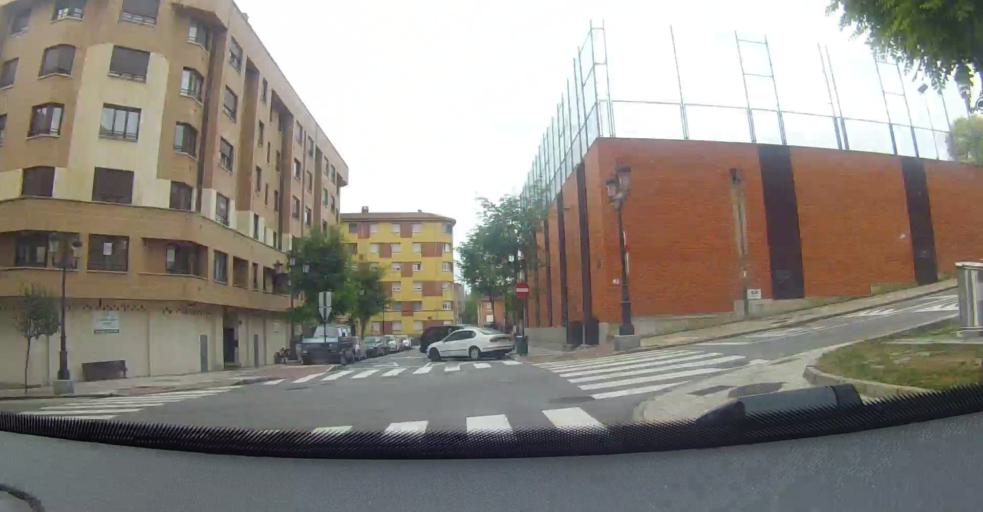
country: ES
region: Asturias
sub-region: Province of Asturias
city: Oviedo
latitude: 43.3702
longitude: -5.8564
